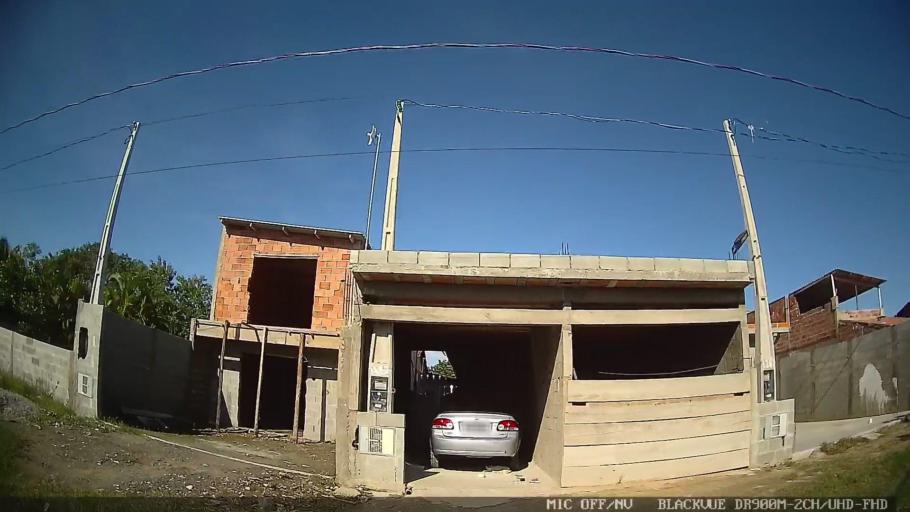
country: BR
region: Sao Paulo
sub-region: Itanhaem
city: Itanhaem
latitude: -24.2252
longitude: -46.8797
